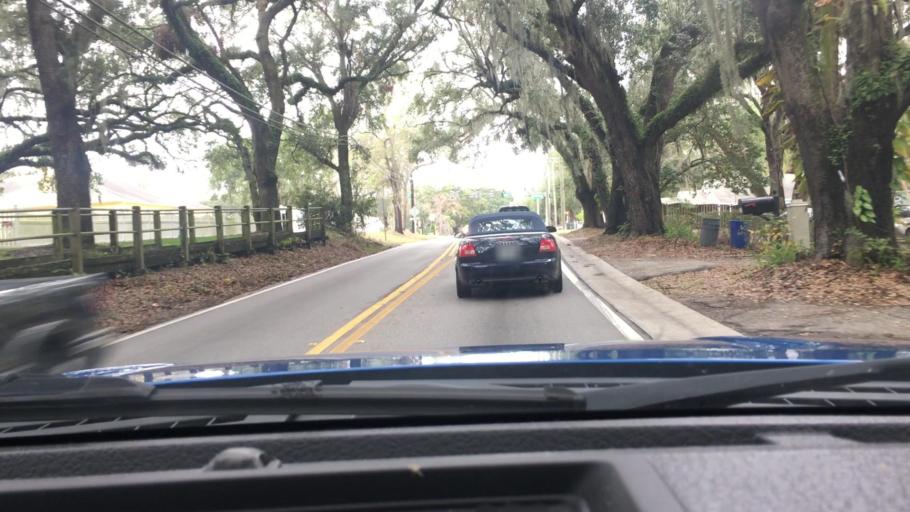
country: US
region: Florida
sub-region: Hillsborough County
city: Mango
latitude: 27.9585
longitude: -82.3104
